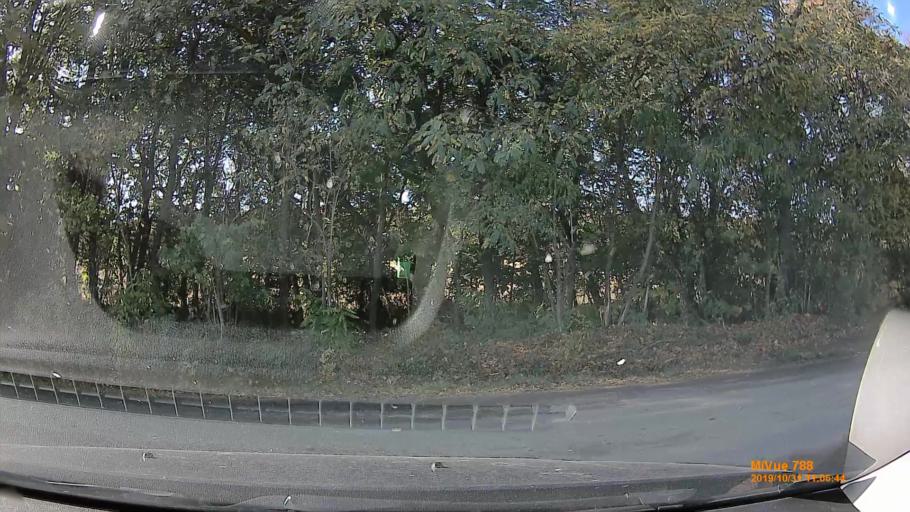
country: HU
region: Pest
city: Pilisborosjeno
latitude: 47.6006
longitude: 18.9951
